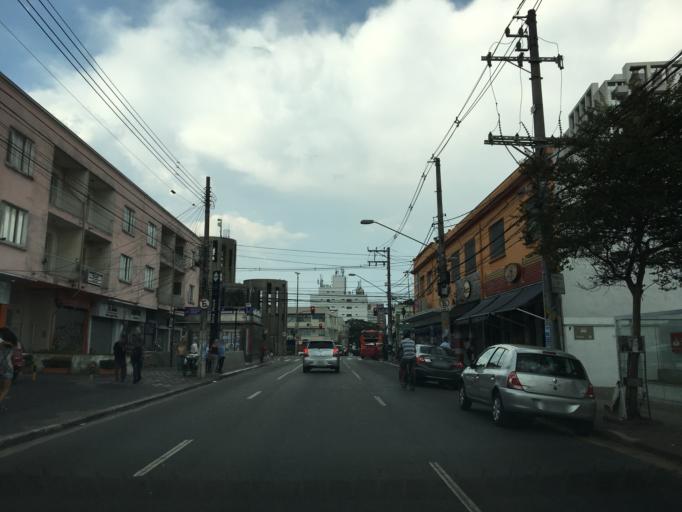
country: BR
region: Sao Paulo
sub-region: Sao Paulo
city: Sao Paulo
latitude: -23.5819
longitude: -46.6394
